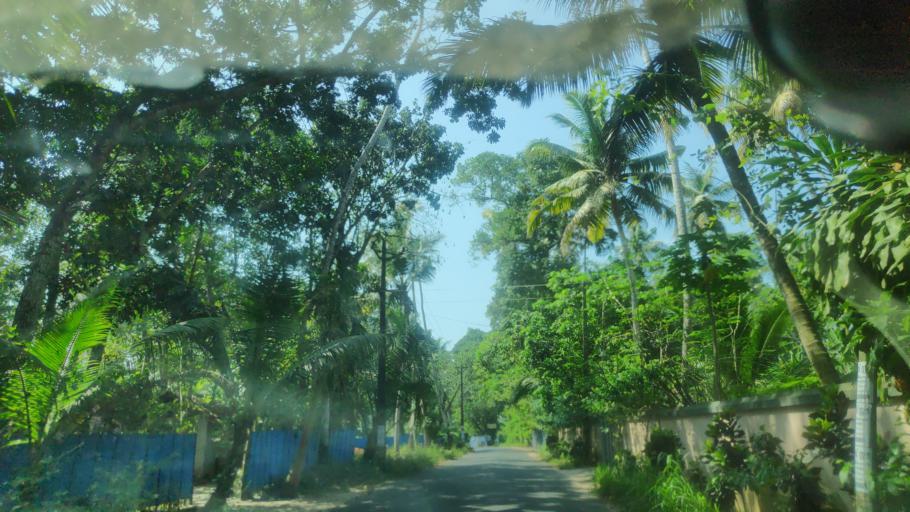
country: IN
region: Kerala
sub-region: Alappuzha
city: Vayalar
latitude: 9.6634
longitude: 76.3084
